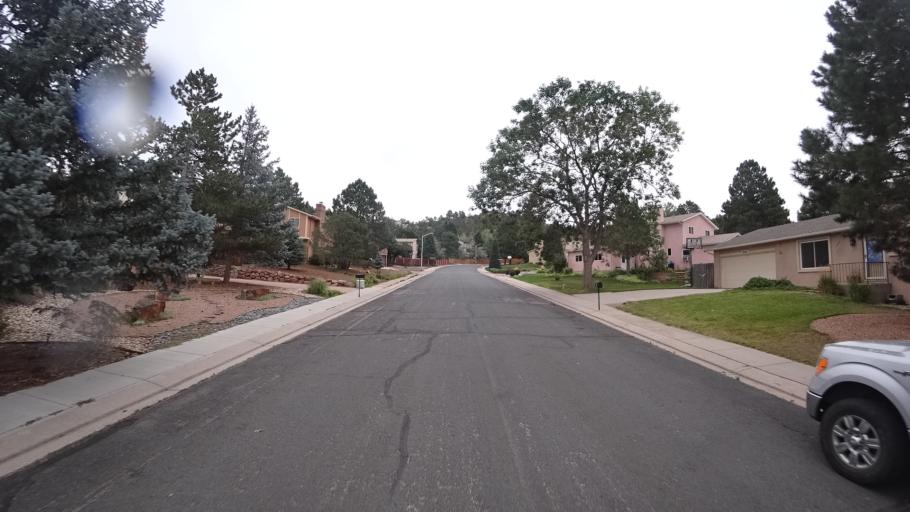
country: US
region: Colorado
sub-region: El Paso County
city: Colorado Springs
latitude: 38.9211
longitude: -104.8108
